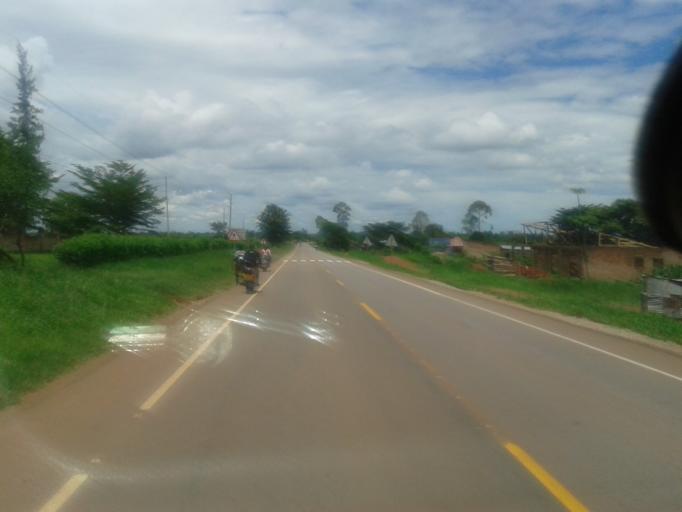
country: UG
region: Western Region
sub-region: Kiryandongo District
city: Kiryandongo
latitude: 1.7891
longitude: 32.0148
